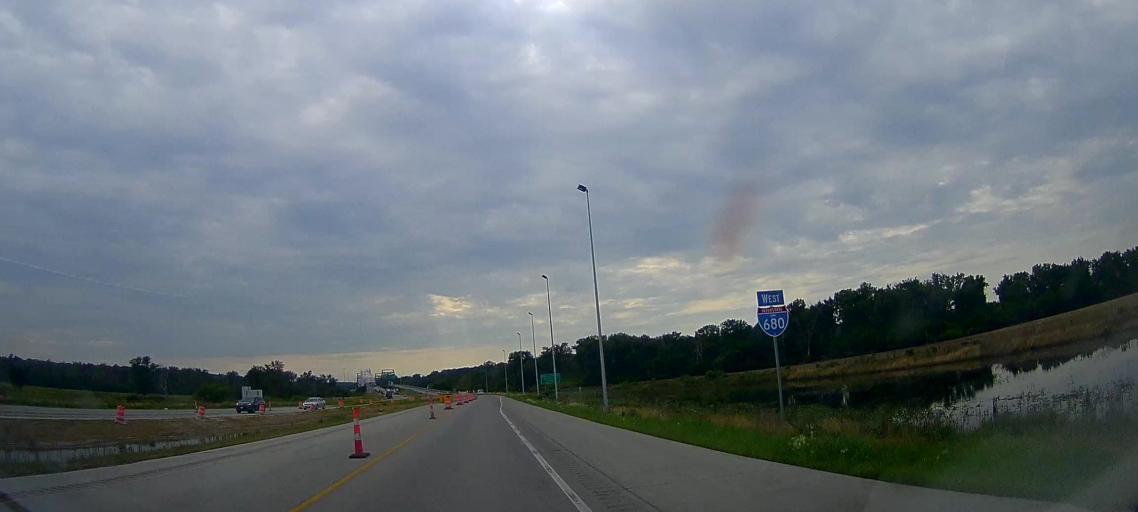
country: US
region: Iowa
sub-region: Pottawattamie County
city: Carter Lake
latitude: 41.3468
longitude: -95.9473
